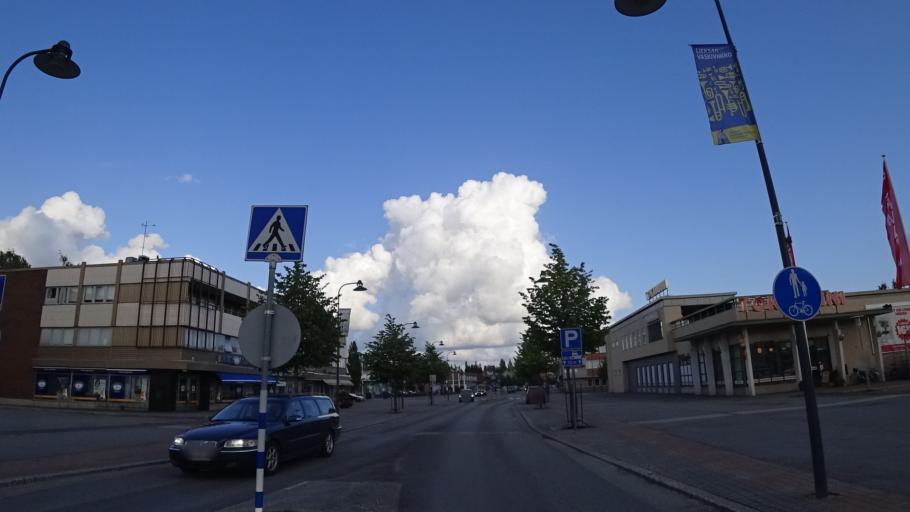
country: FI
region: North Karelia
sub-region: Pielisen Karjala
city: Lieksa
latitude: 63.3189
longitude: 30.0247
